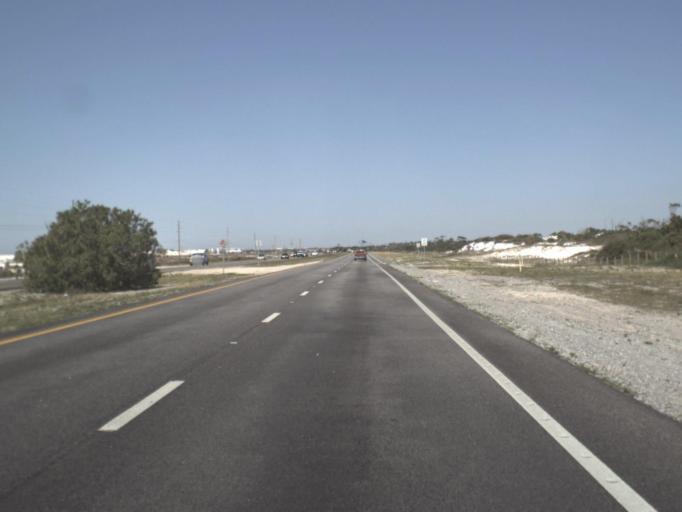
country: US
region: Florida
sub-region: Okaloosa County
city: Destin
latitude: 30.3918
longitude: -86.5449
